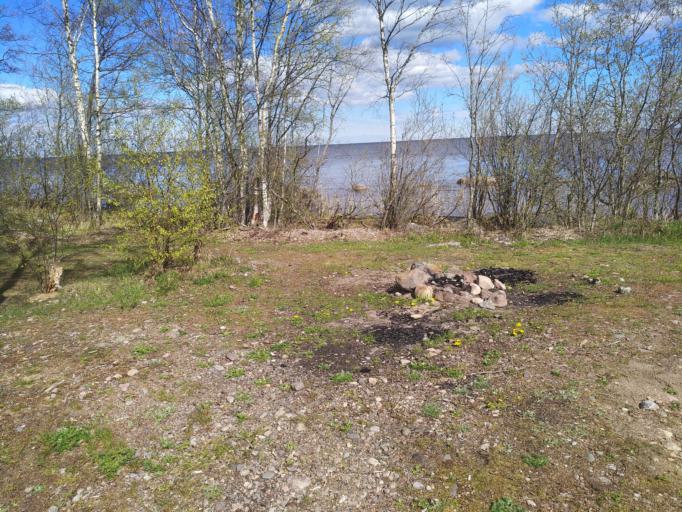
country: RU
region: Leningrad
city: Garbolovo
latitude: 60.5745
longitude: 30.6764
